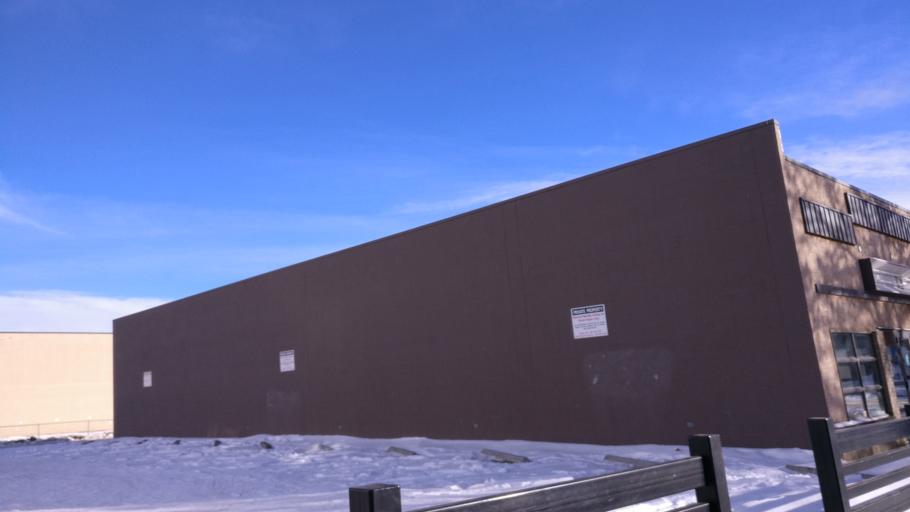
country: CA
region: Alberta
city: Red Deer
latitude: 52.2665
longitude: -113.8140
